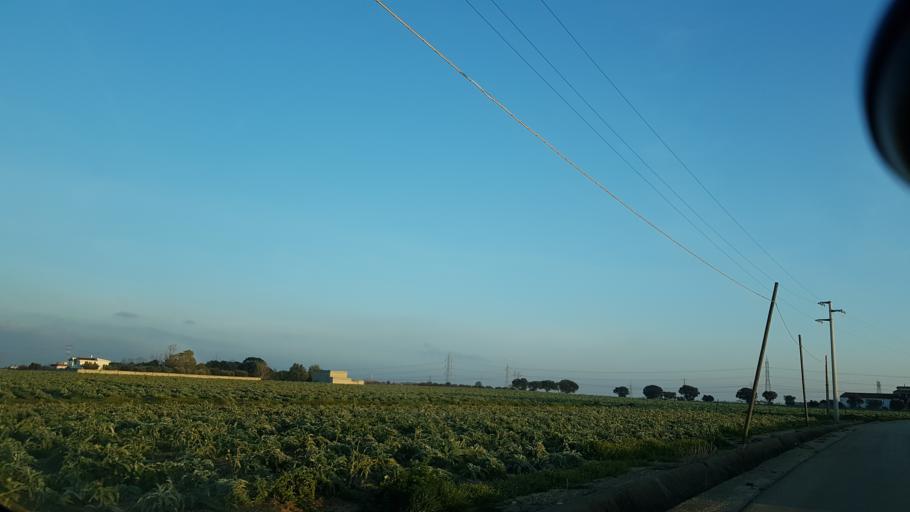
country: IT
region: Apulia
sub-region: Provincia di Brindisi
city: La Rosa
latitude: 40.6055
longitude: 17.9388
